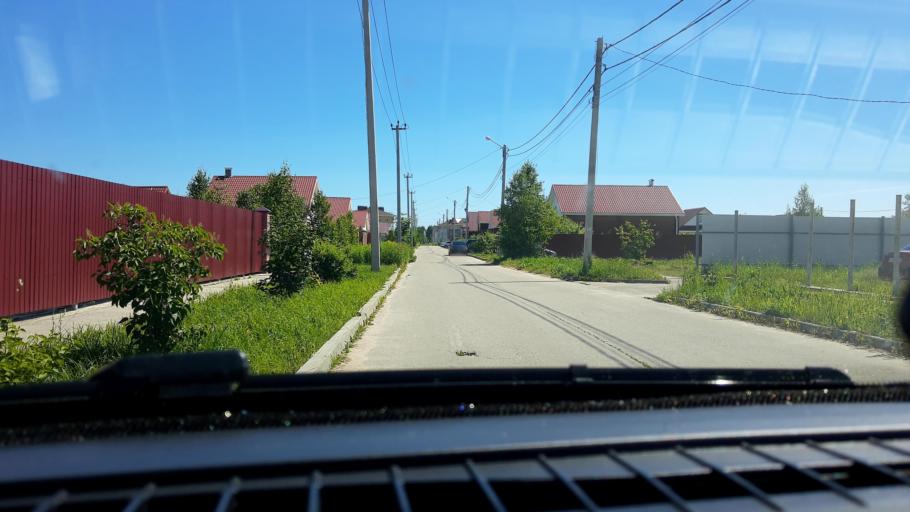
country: RU
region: Nizjnij Novgorod
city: Bor
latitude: 56.3910
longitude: 44.0528
